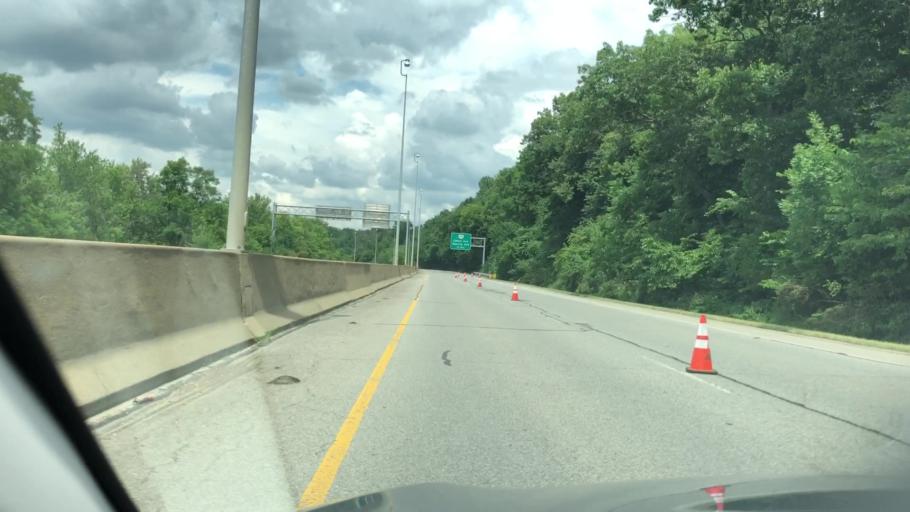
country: US
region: Ohio
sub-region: Stark County
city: Massillon
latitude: 40.7753
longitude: -81.5175
